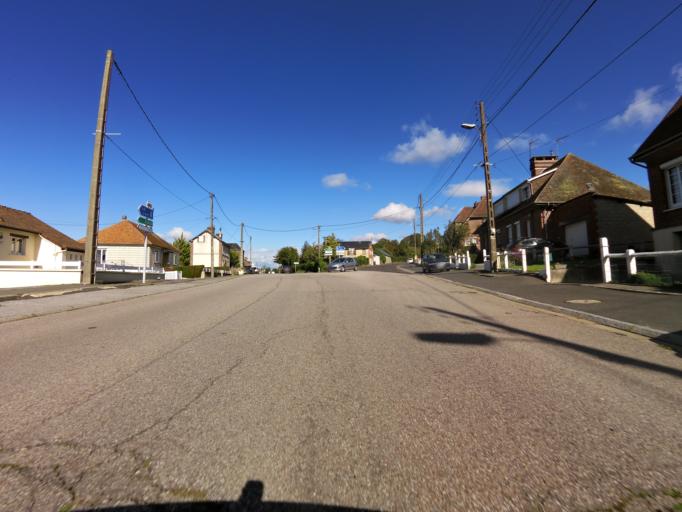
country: FR
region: Lower Normandy
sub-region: Departement de l'Orne
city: Vimoutiers
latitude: 48.9341
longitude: 0.2003
